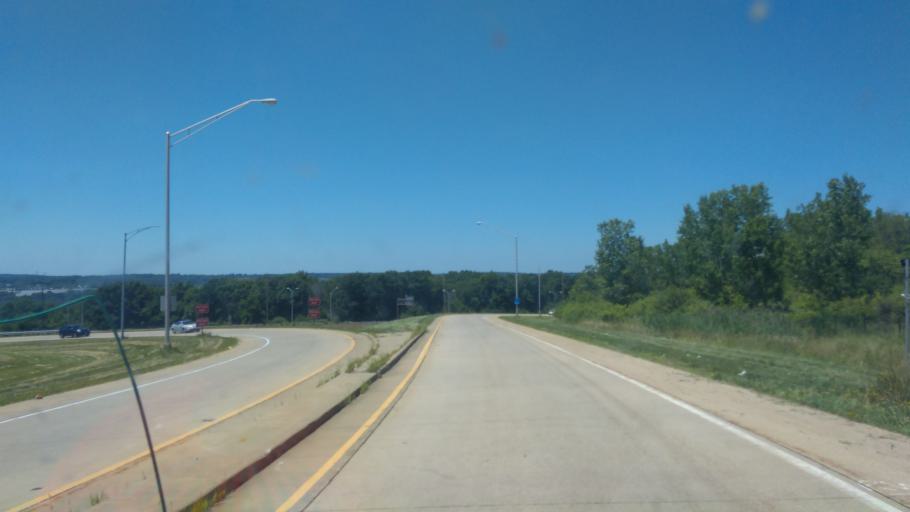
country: US
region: Ohio
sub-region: Trumbull County
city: Churchill
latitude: 41.1355
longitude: -80.6756
